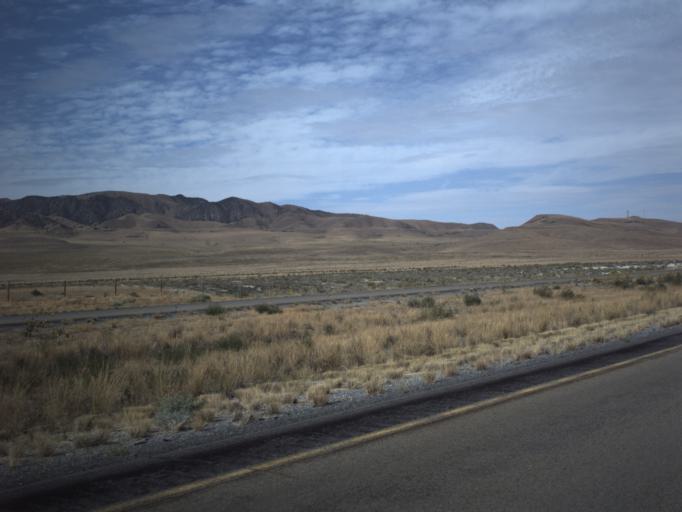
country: US
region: Utah
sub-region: Tooele County
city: Grantsville
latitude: 40.7851
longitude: -112.8217
